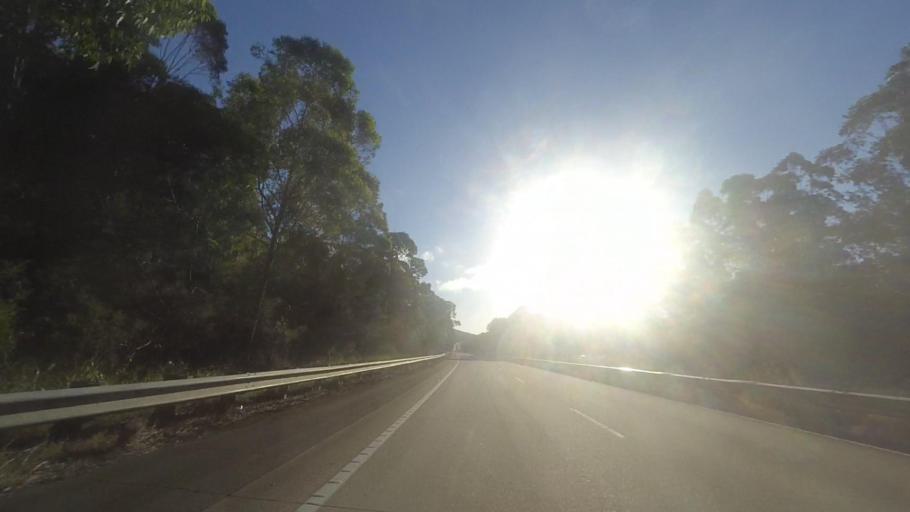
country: AU
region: New South Wales
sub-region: Great Lakes
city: Bulahdelah
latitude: -32.3763
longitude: 152.2759
